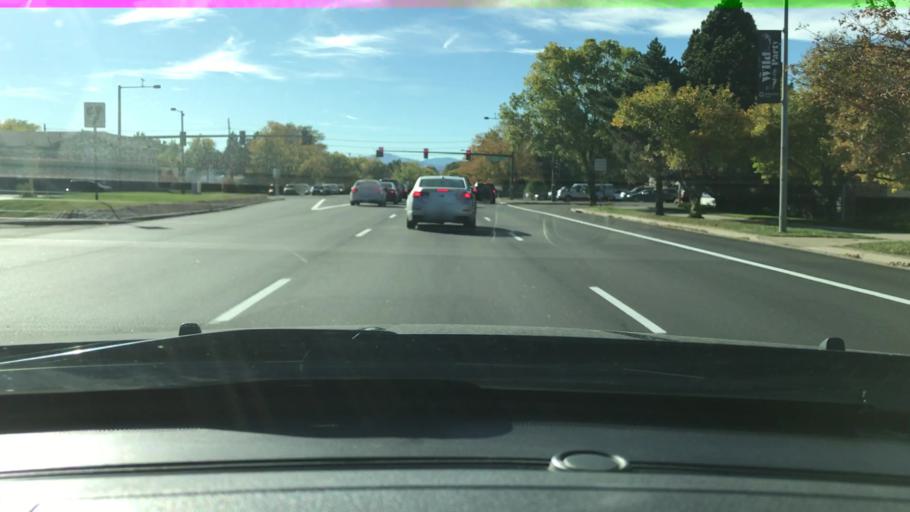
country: US
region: Colorado
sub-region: Arapahoe County
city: Glendale
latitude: 39.7114
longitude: -104.9117
